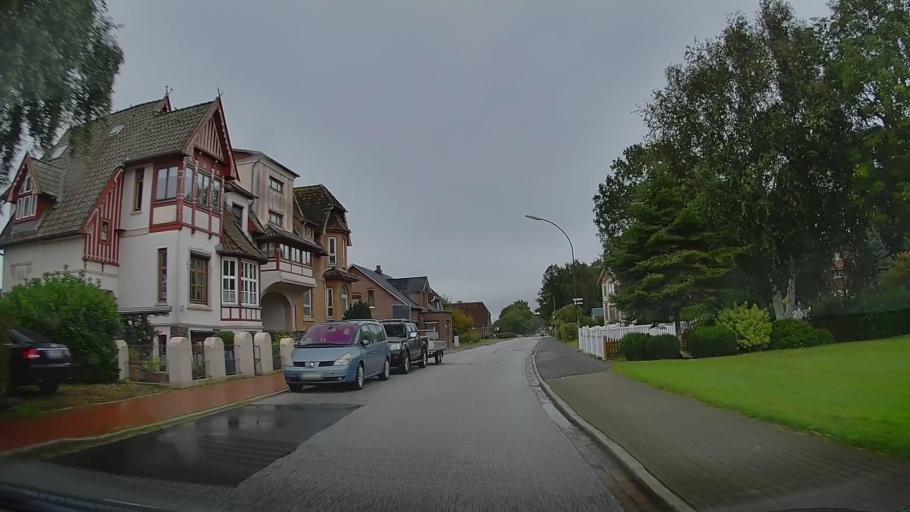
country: DE
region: Schleswig-Holstein
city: Sankt Margarethen
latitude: 53.8923
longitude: 9.2536
